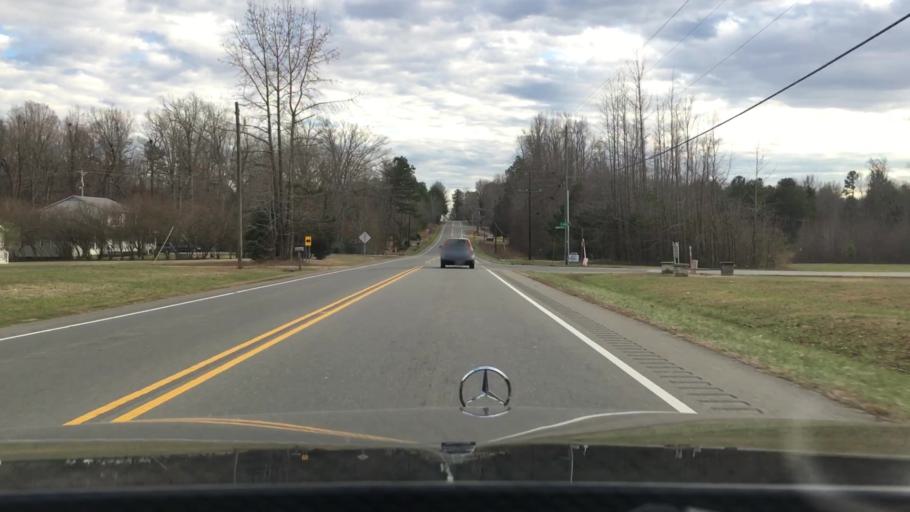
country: US
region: North Carolina
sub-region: Orange County
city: Hillsborough
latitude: 36.1353
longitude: -79.1201
